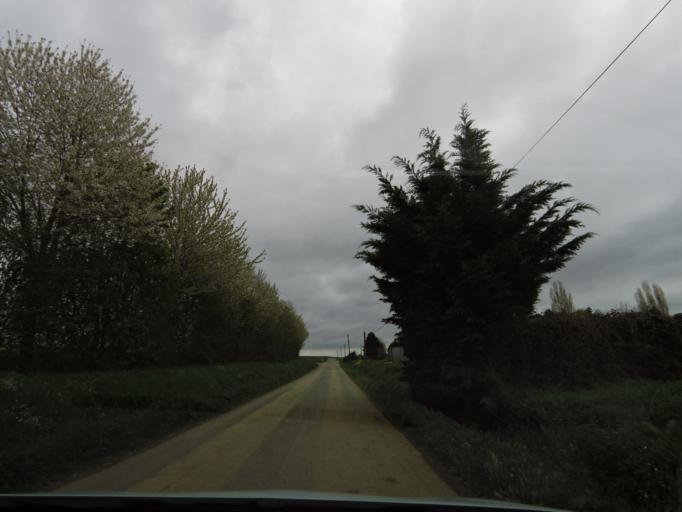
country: FR
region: Brittany
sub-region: Departement d'Ille-et-Vilaine
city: Janze
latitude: 47.9612
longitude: -1.5374
